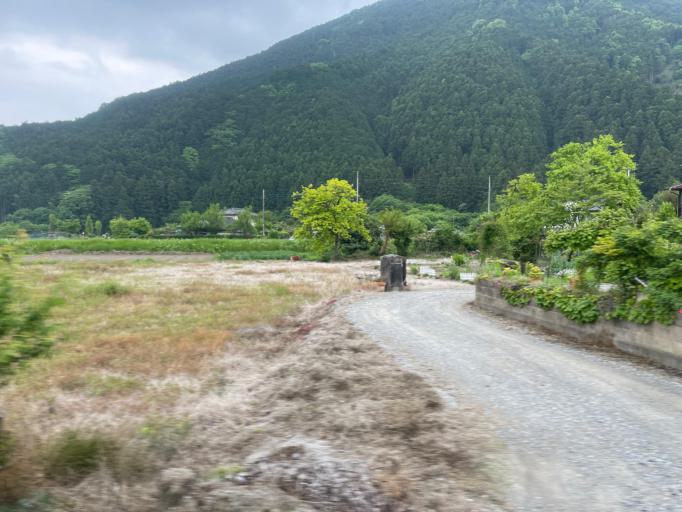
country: JP
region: Tochigi
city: Tanuma
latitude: 36.4703
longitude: 139.6309
